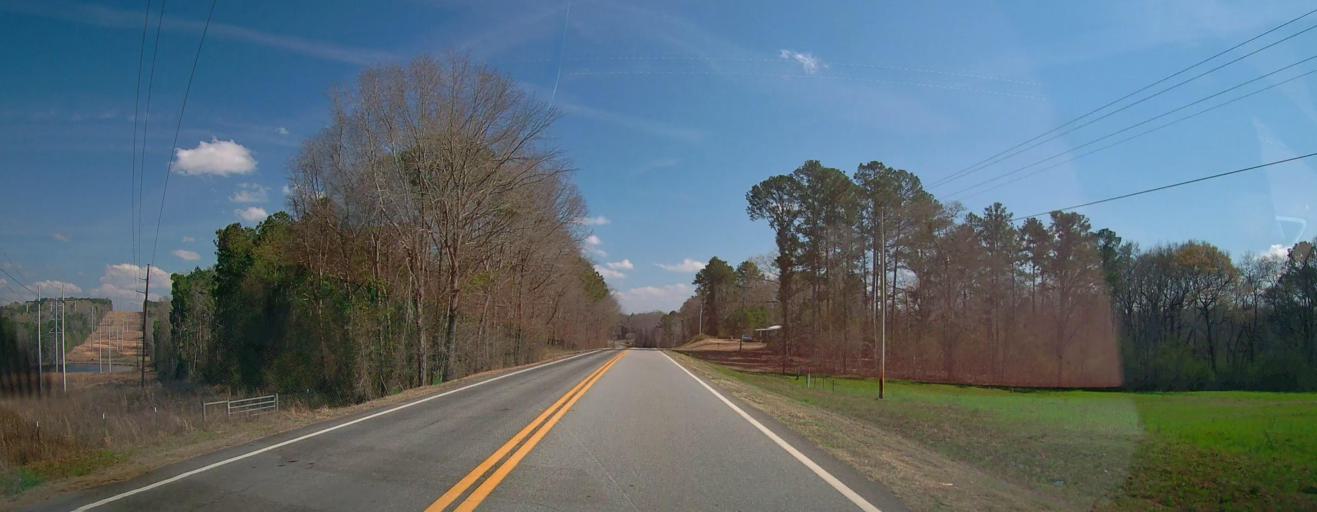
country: US
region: Georgia
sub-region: Wilkinson County
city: Gordon
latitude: 32.9055
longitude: -83.3761
